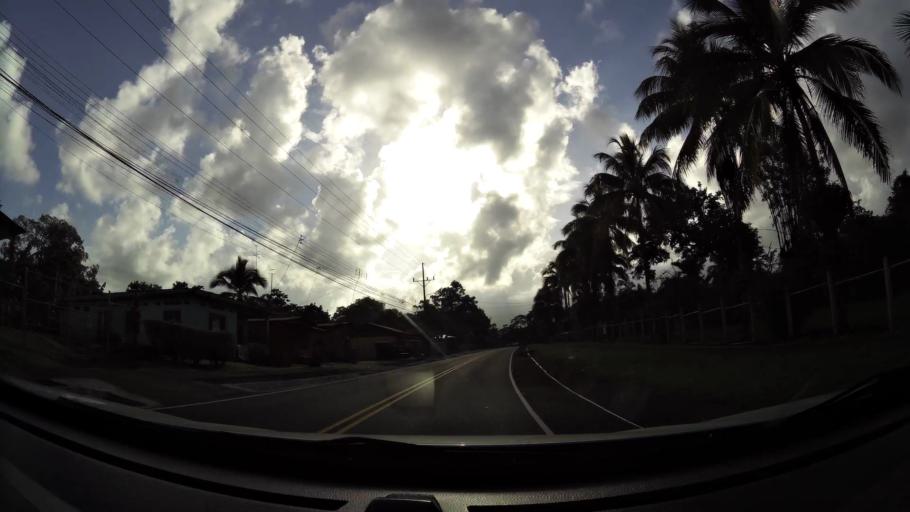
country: CR
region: Limon
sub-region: Canton de Siquirres
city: Siquirres
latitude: 10.0872
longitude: -83.5433
